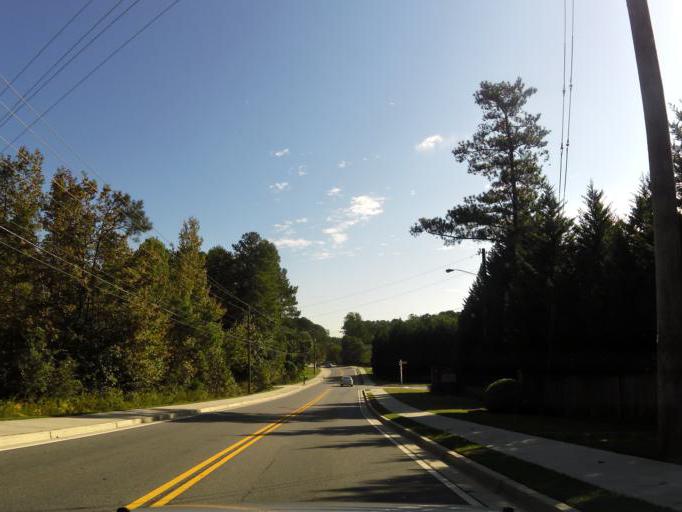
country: US
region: Georgia
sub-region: Cobb County
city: Acworth
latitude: 34.0430
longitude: -84.6722
